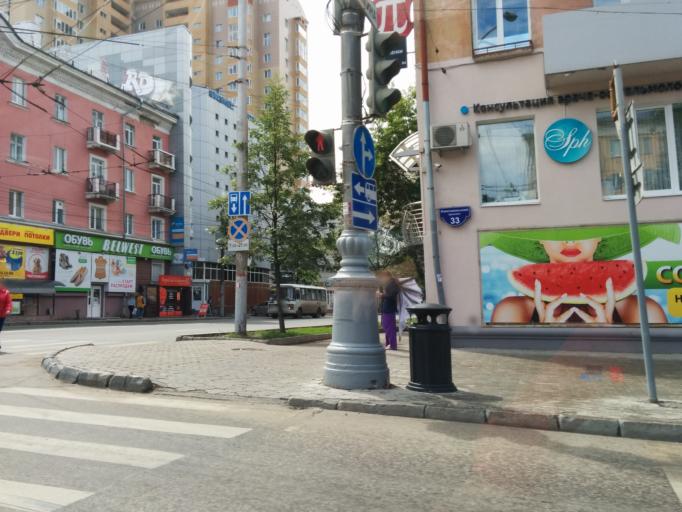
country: RU
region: Perm
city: Perm
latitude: 58.0065
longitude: 56.2430
